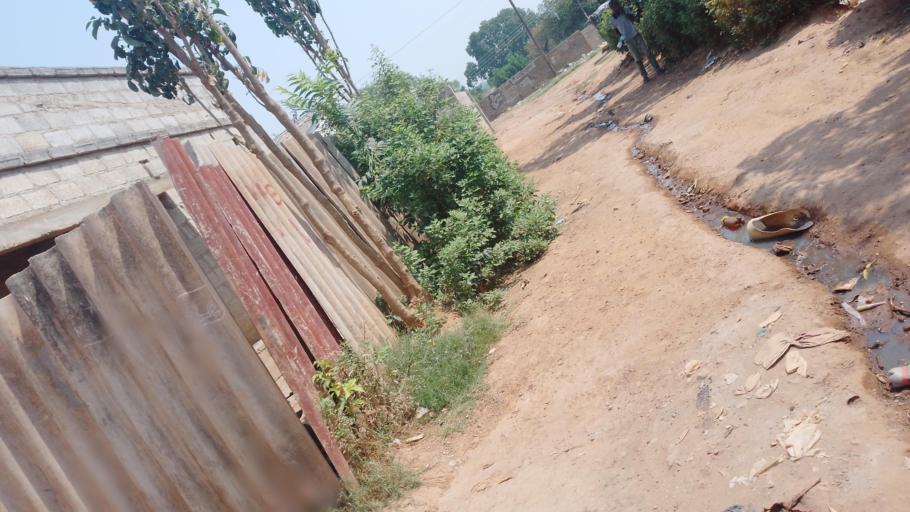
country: ZM
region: Lusaka
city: Lusaka
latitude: -15.3942
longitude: 28.3740
